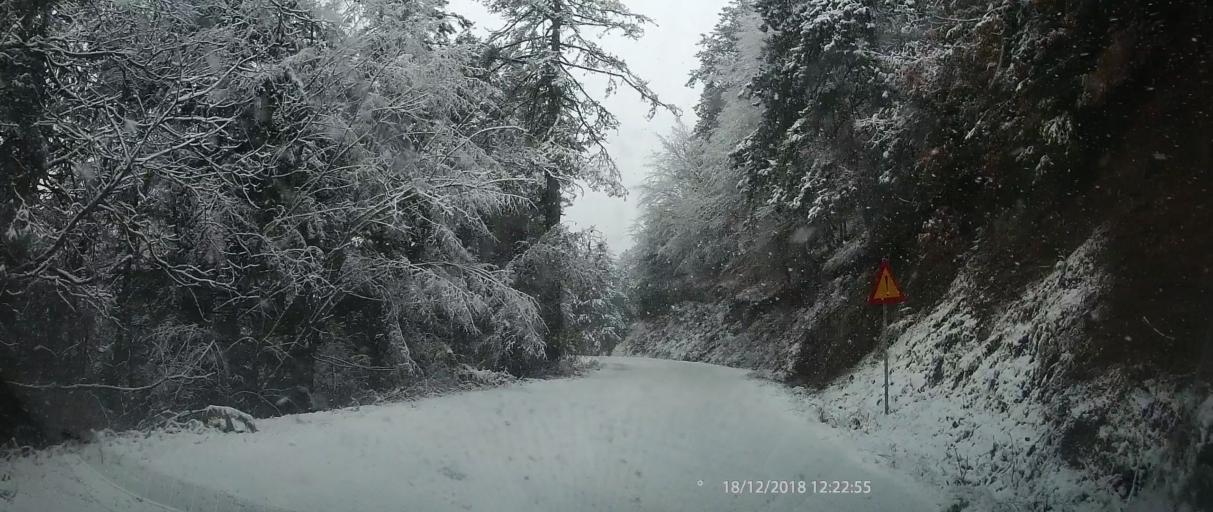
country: GR
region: Central Macedonia
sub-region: Nomos Pierias
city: Litochoro
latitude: 40.0931
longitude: 22.4198
